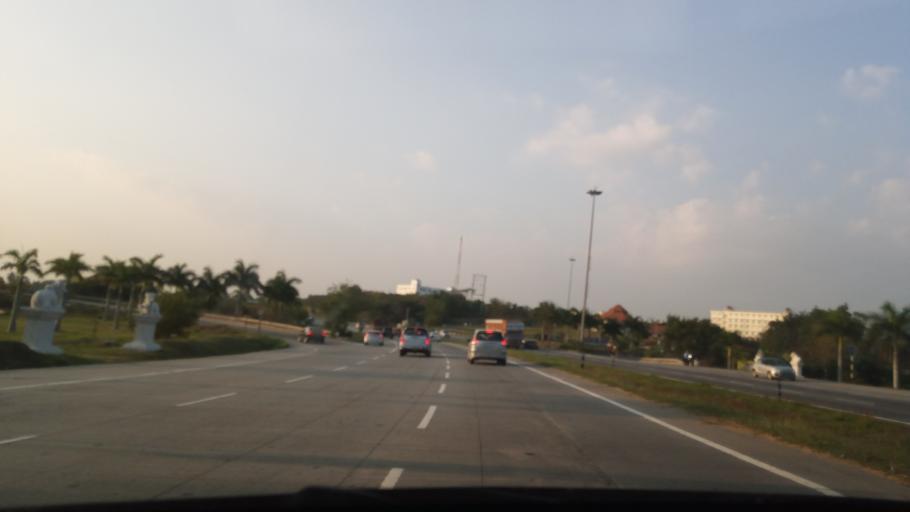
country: IN
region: Karnataka
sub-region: Bangalore Urban
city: Bangalore
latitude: 12.8790
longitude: 77.4948
